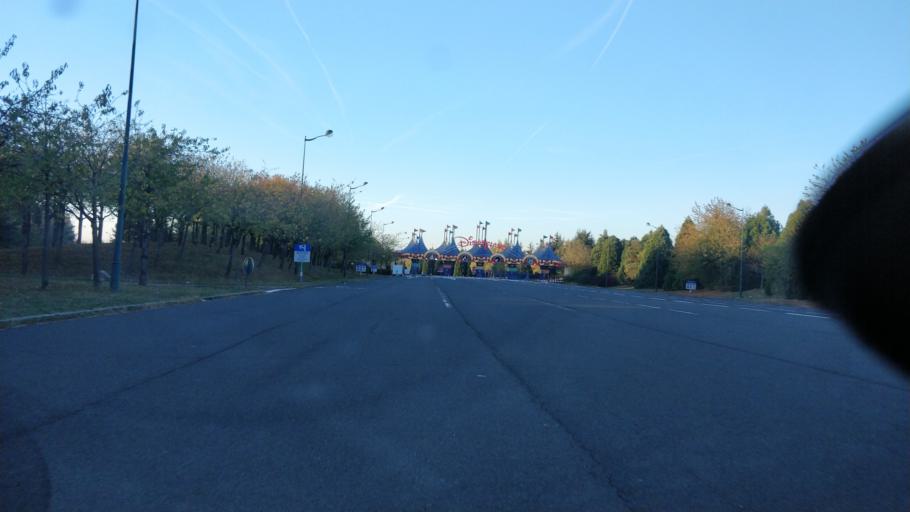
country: FR
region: Ile-de-France
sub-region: Departement de Seine-et-Marne
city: Coupvray
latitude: 48.8745
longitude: 2.7971
